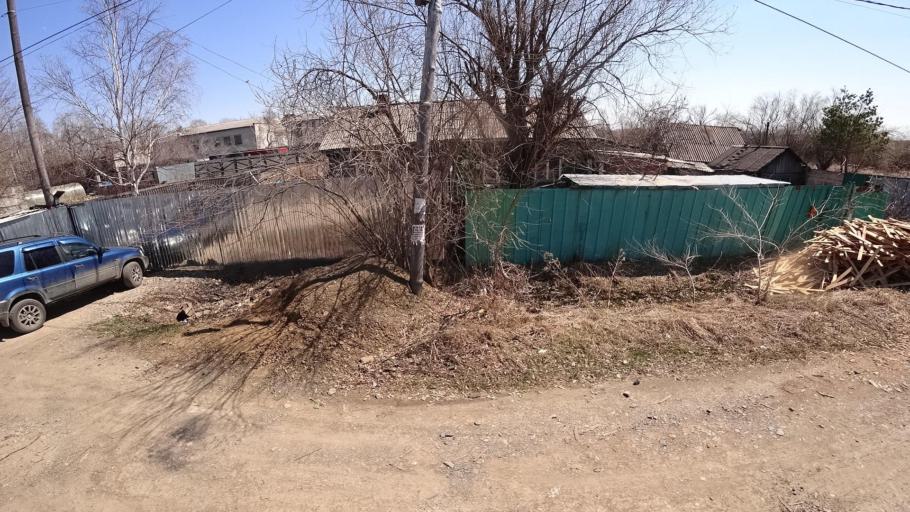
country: RU
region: Khabarovsk Krai
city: Khurba
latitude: 50.4043
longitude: 136.8841
